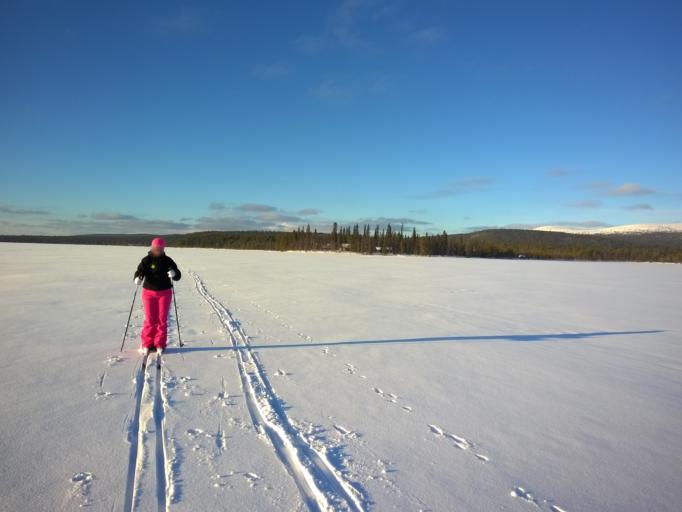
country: FI
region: Lapland
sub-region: Tunturi-Lappi
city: Muonio
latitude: 67.9306
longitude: 24.0467
